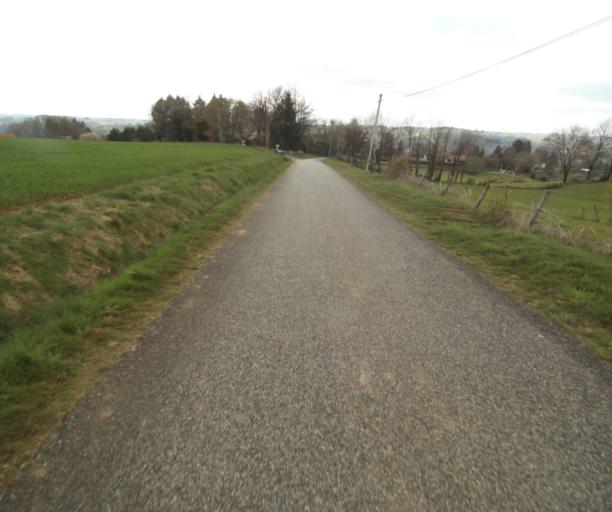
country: FR
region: Limousin
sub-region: Departement de la Correze
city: Naves
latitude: 45.3069
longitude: 1.8135
